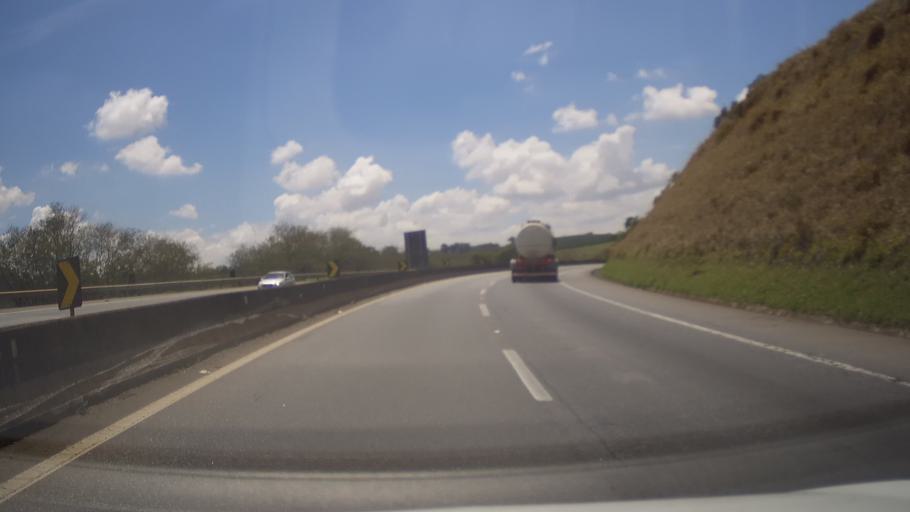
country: BR
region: Minas Gerais
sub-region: Sao Goncalo Do Sapucai
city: Sao Goncalo do Sapucai
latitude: -21.9092
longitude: -45.5715
